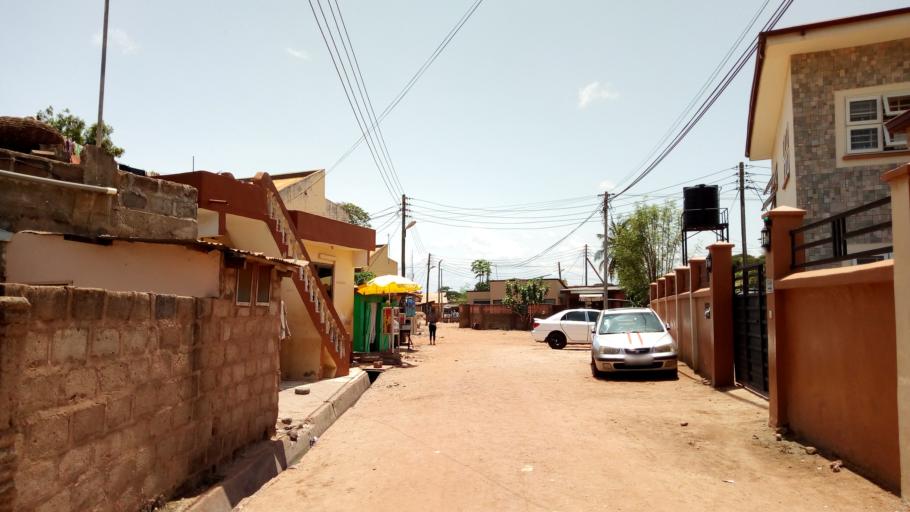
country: GH
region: Greater Accra
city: Tema
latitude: 5.6397
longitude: -0.0028
